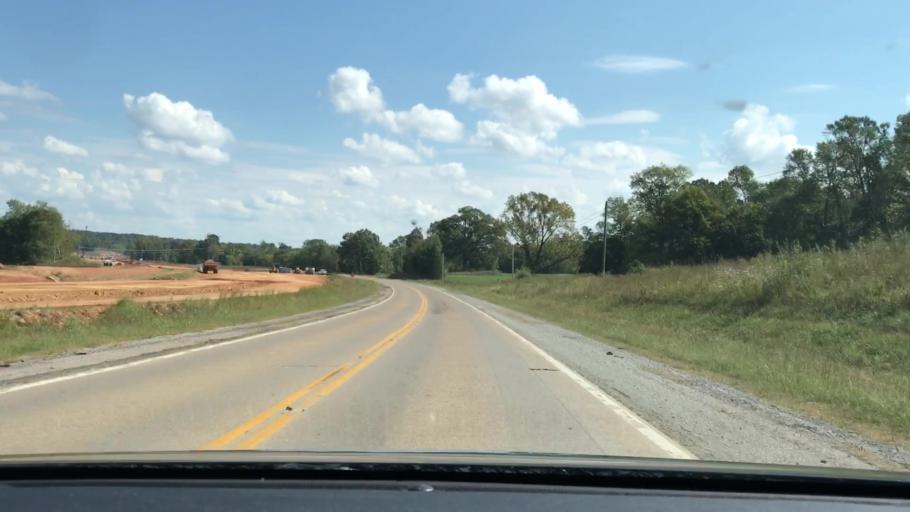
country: US
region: Kentucky
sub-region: Trigg County
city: Cadiz
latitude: 36.7984
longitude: -87.9479
